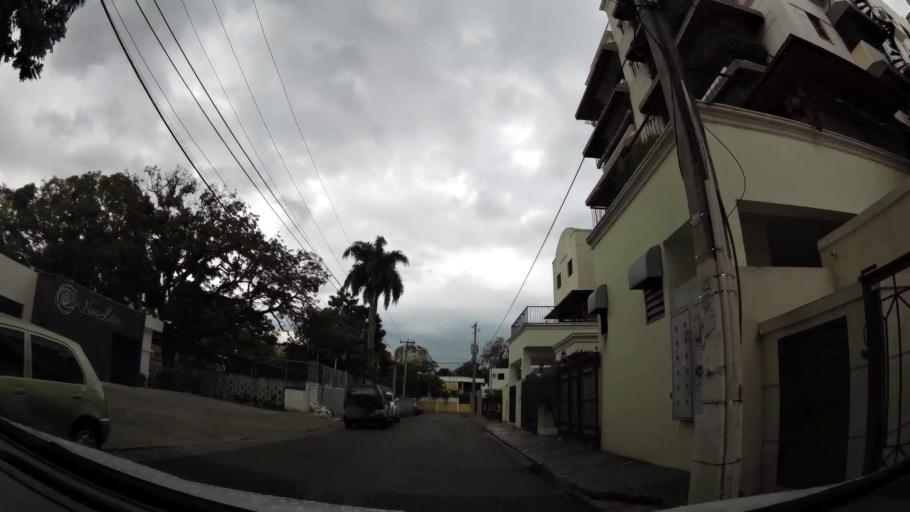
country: DO
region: Nacional
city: La Agustina
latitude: 18.4880
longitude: -69.9372
